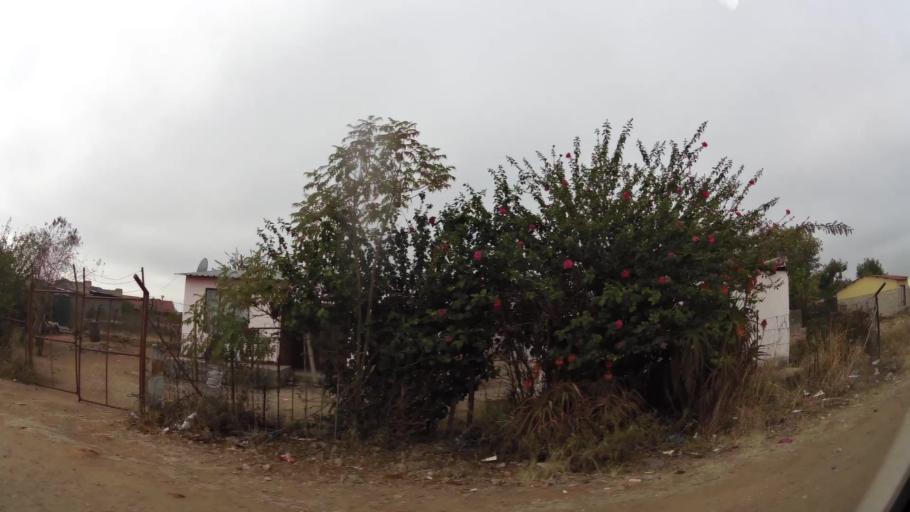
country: ZA
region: Limpopo
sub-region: Capricorn District Municipality
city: Polokwane
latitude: -23.8336
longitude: 29.3813
